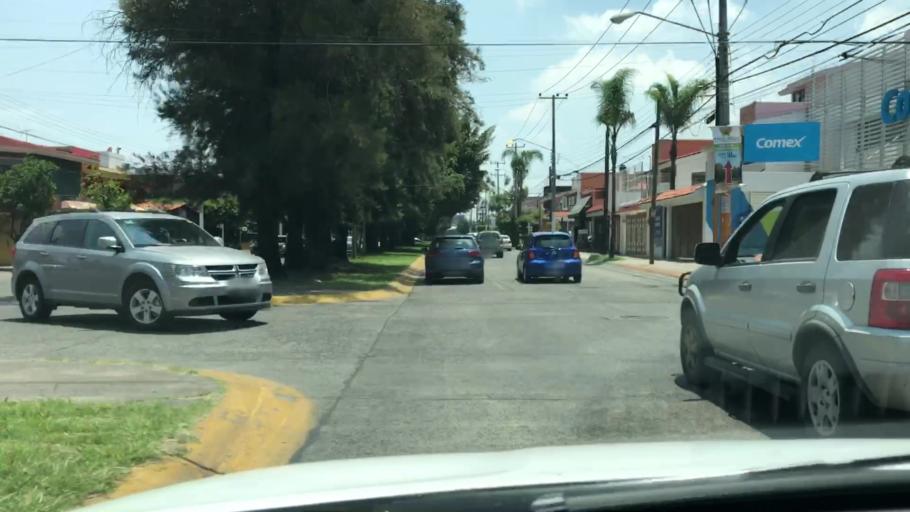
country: MX
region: Jalisco
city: Guadalajara
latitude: 20.6735
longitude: -103.4304
